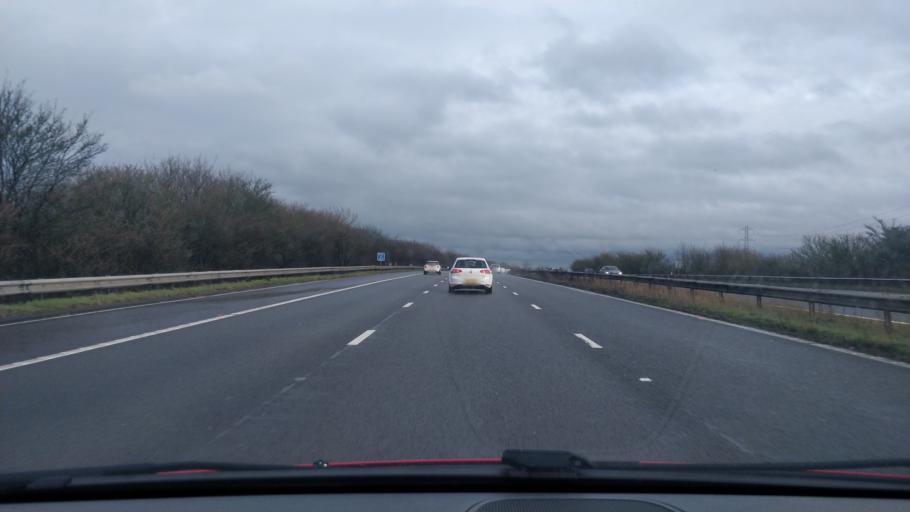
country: GB
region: England
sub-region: Sefton
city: Melling
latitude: 53.4847
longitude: -2.9238
